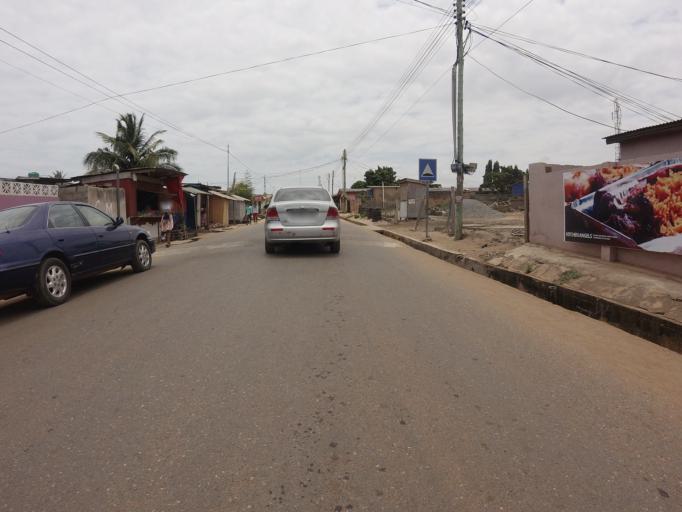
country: GH
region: Greater Accra
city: Nungua
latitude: 5.6062
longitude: -0.0980
